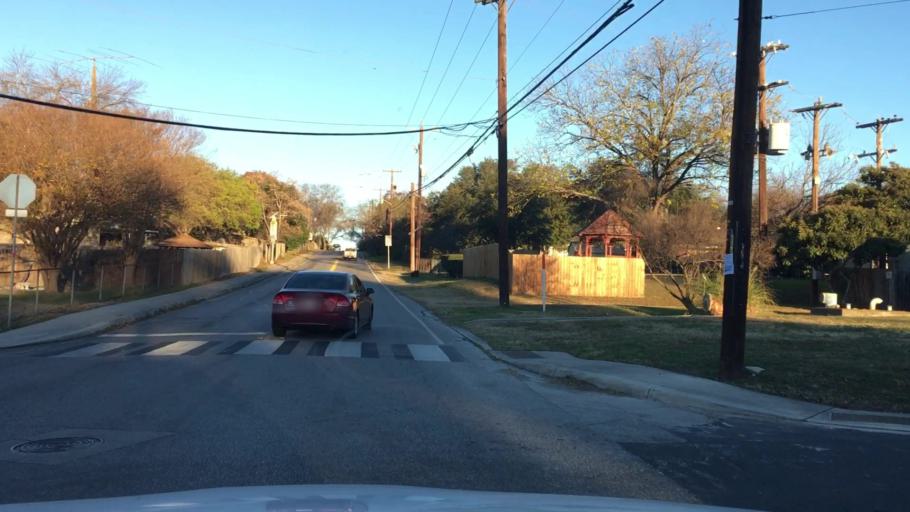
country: US
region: Texas
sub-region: Bexar County
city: Castle Hills
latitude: 29.5349
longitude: -98.5012
